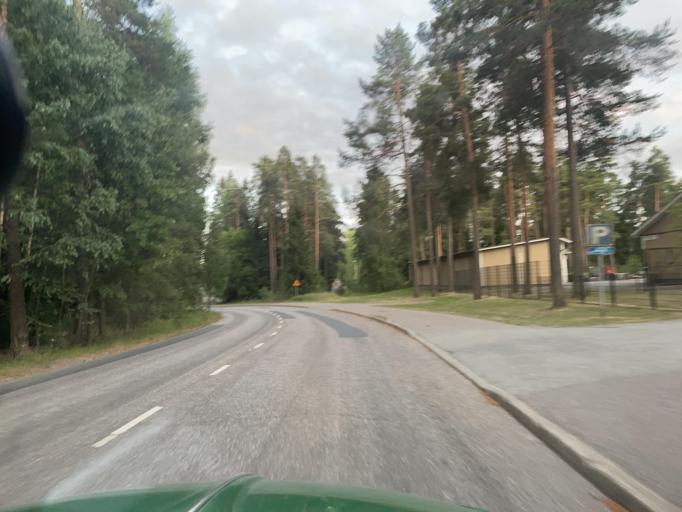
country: FI
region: Uusimaa
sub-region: Helsinki
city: Lohja
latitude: 60.2392
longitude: 24.0683
